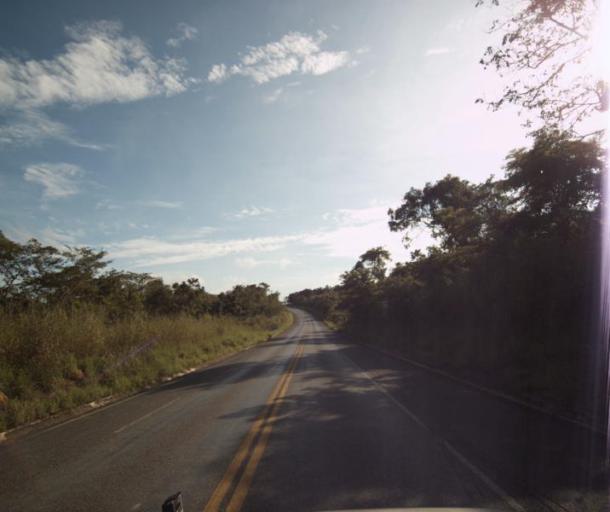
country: BR
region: Goias
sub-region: Pirenopolis
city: Pirenopolis
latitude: -15.5722
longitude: -48.6230
